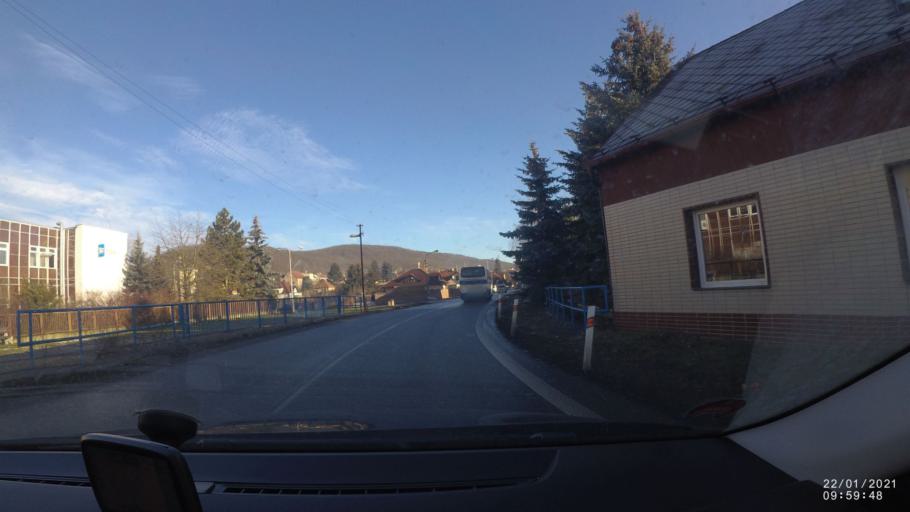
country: CZ
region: Central Bohemia
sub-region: Okres Beroun
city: Lodenice
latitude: 49.9966
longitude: 14.1590
